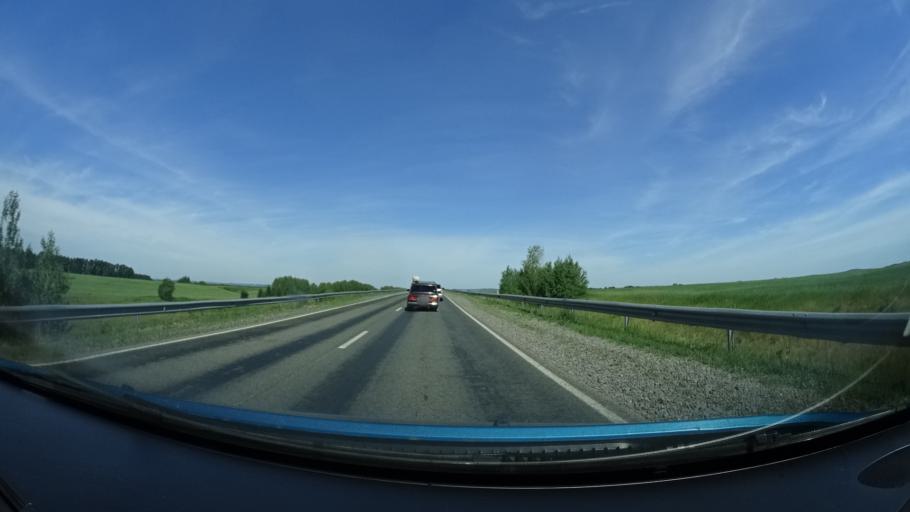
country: RU
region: Bashkortostan
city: Blagoveshchensk
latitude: 55.1934
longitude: 55.8368
